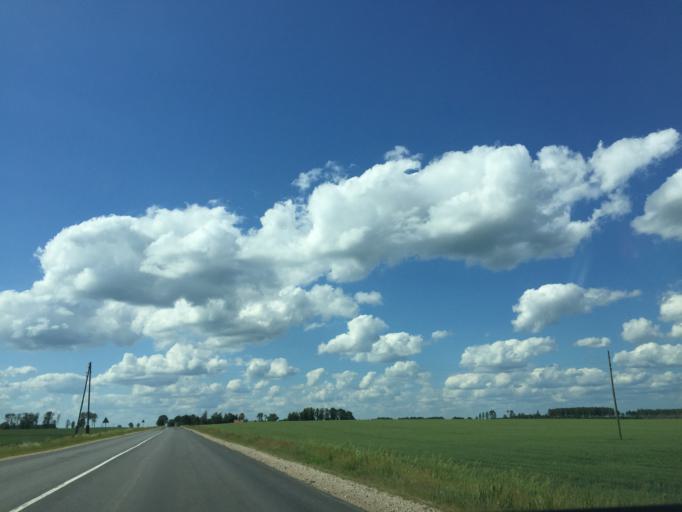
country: LV
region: Engure
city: Smarde
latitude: 56.8551
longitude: 23.3002
